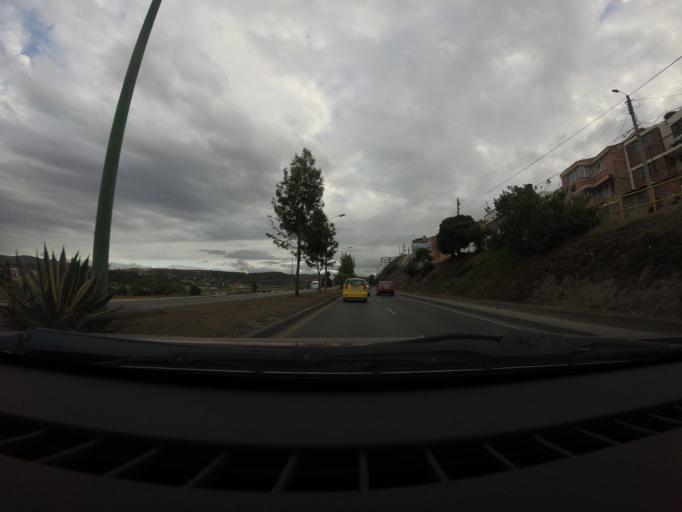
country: CO
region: Boyaca
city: Tunja
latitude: 5.5375
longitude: -73.3560
